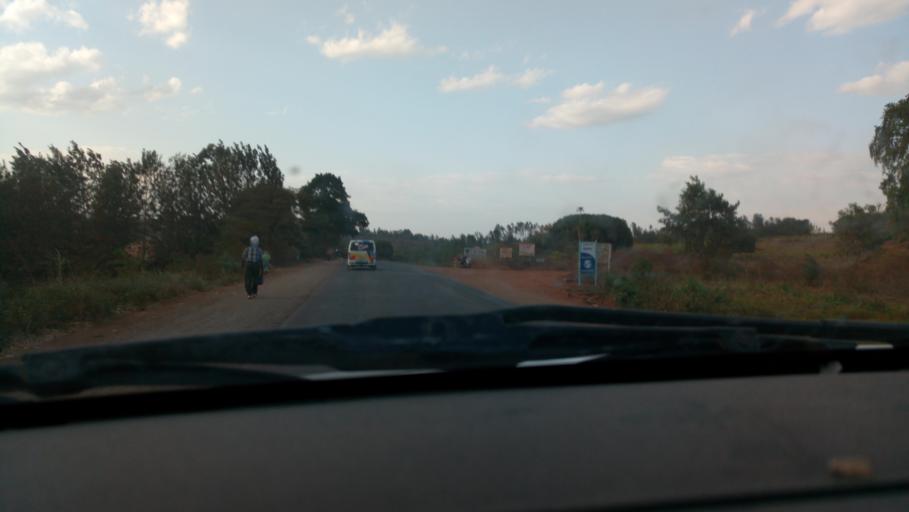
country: KE
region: Murang'a District
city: Maragua
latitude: -0.7610
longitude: 37.1547
